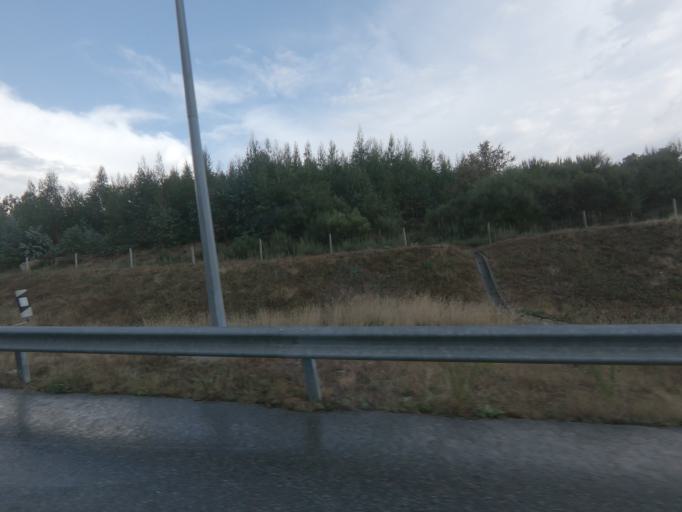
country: PT
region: Viseu
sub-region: Castro Daire
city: Castro Daire
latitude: 40.9643
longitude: -7.8890
